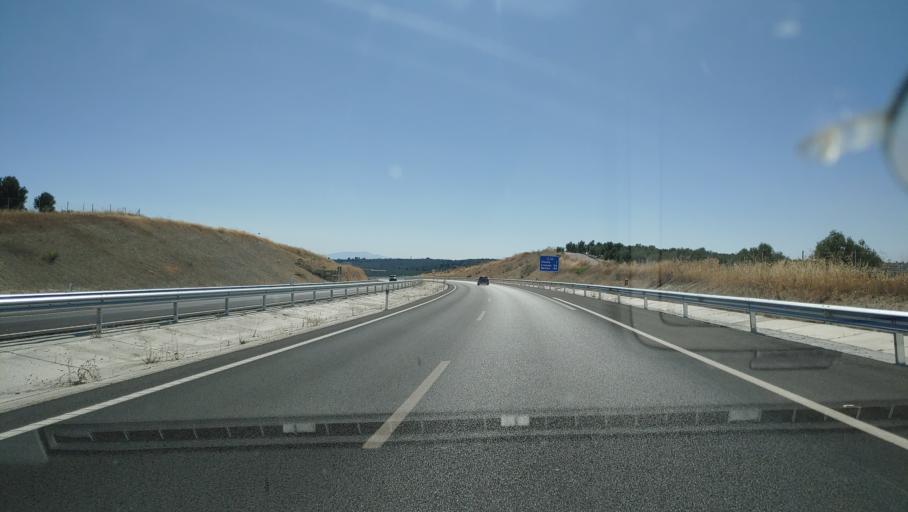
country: ES
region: Andalusia
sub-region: Provincia de Jaen
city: Torreperogil
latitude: 38.0494
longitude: -3.3057
